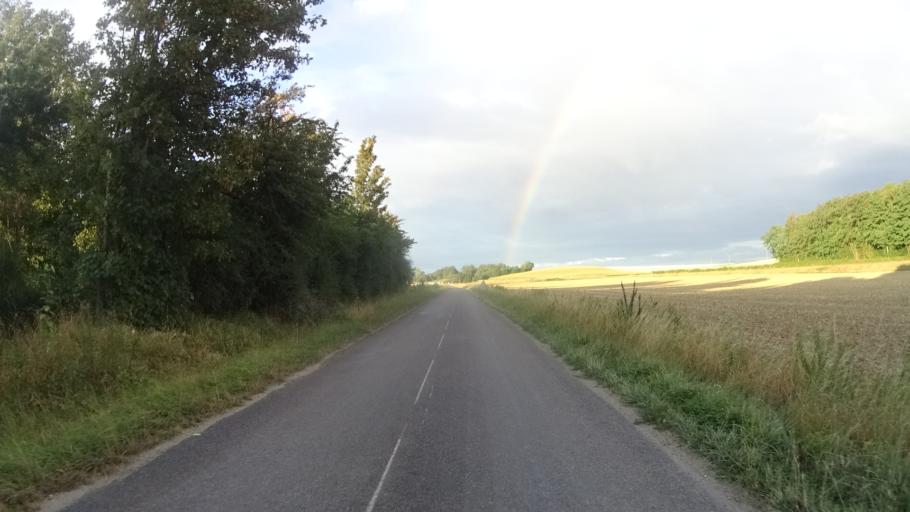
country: FR
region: Bourgogne
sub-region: Departement de Saone-et-Loire
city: Verdun-sur-le-Doubs
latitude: 46.9566
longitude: 5.0703
